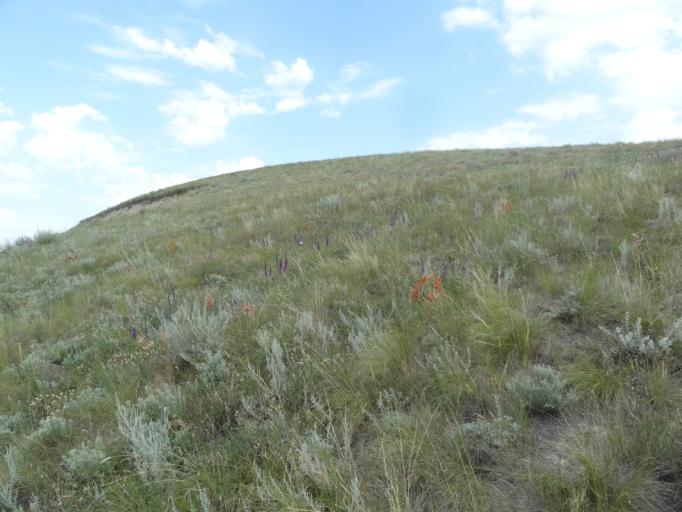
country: RU
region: Saratov
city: Sokolovyy
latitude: 51.4357
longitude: 45.7954
